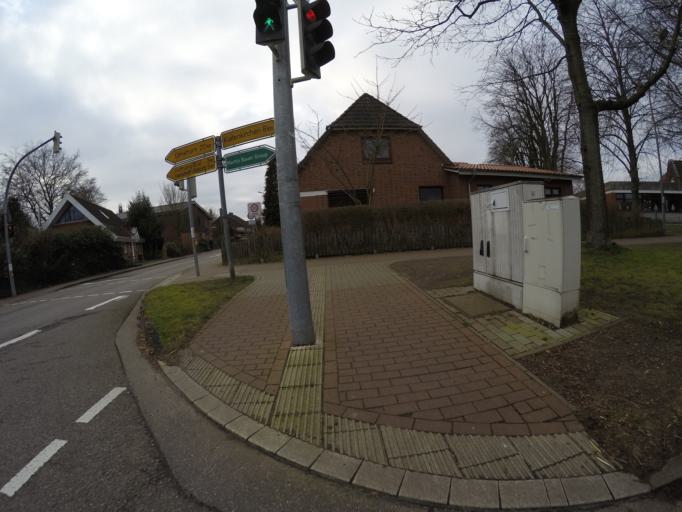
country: DE
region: Schleswig-Holstein
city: Alveslohe
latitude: 53.7898
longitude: 9.9147
